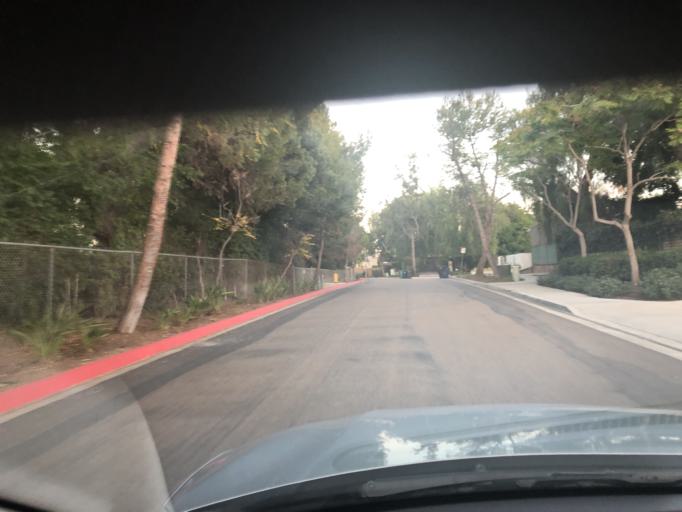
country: US
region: California
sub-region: San Diego County
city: Chula Vista
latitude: 32.6434
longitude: -117.0656
